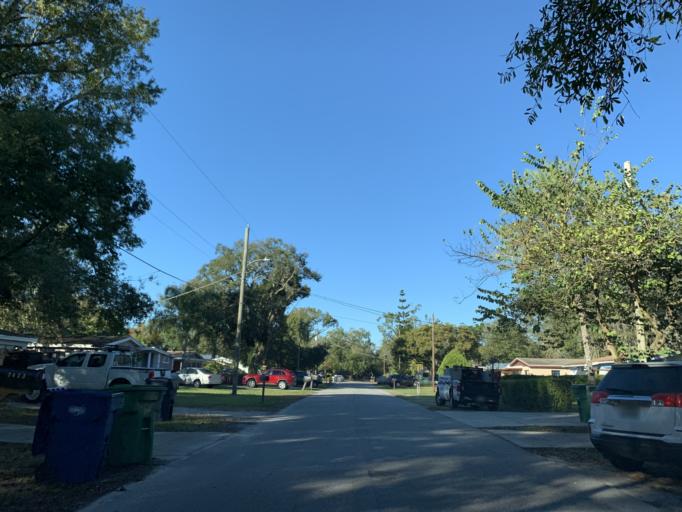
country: US
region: Florida
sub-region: Hillsborough County
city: University
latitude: 28.0348
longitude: -82.4320
